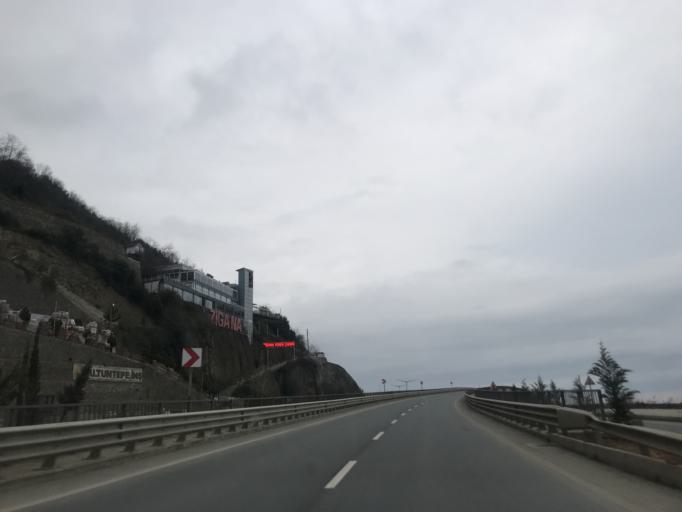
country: TR
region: Trabzon
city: Akcaabat
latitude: 41.0005
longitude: 39.6376
